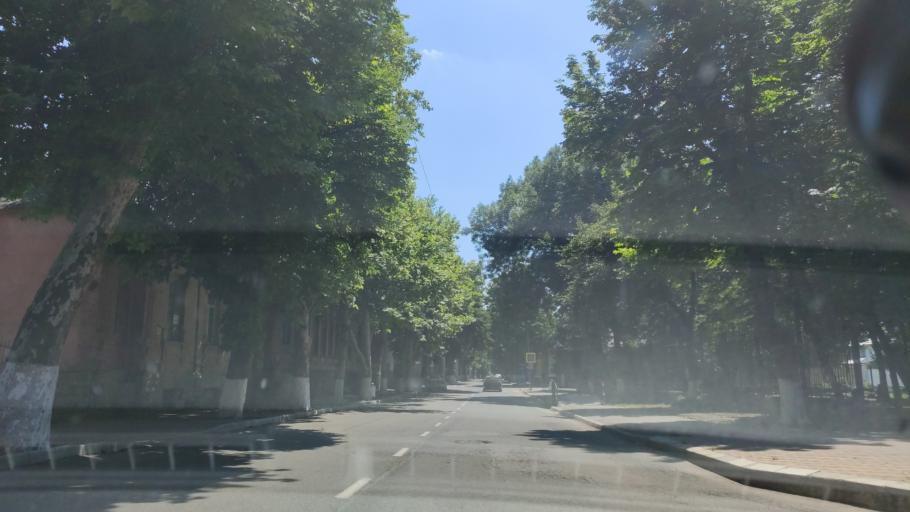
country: MD
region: Raionul Soroca
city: Soroca
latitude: 48.1535
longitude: 28.3002
